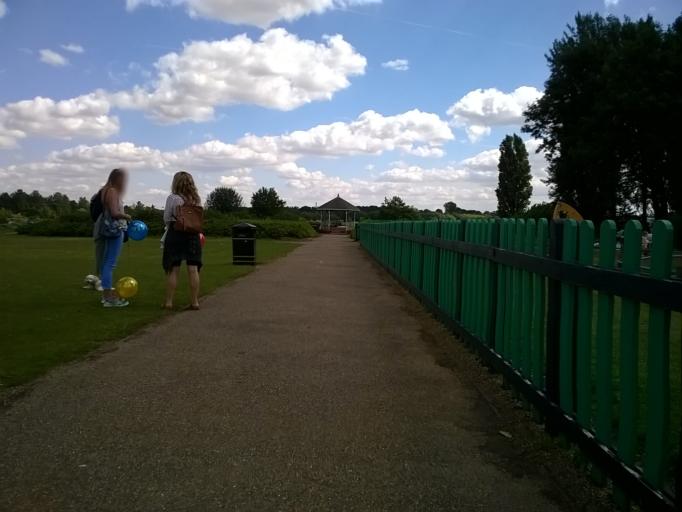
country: GB
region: England
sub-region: Milton Keynes
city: Broughton
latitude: 52.0514
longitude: -0.7223
